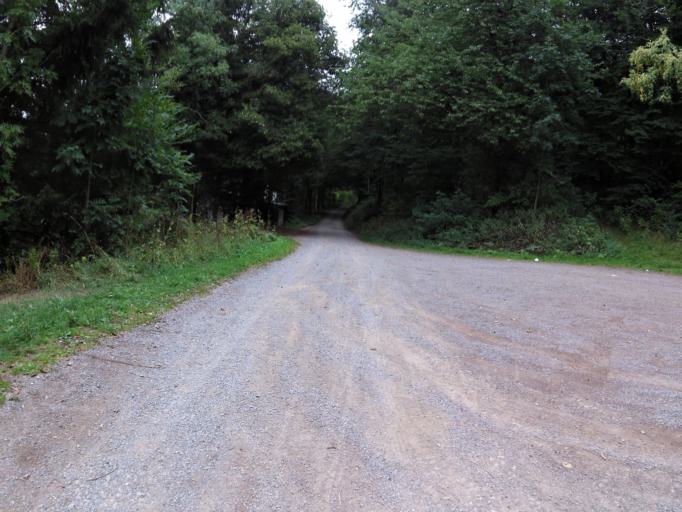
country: DE
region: North Rhine-Westphalia
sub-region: Regierungsbezirk Koln
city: Nettersheim
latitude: 50.5126
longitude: 6.6111
